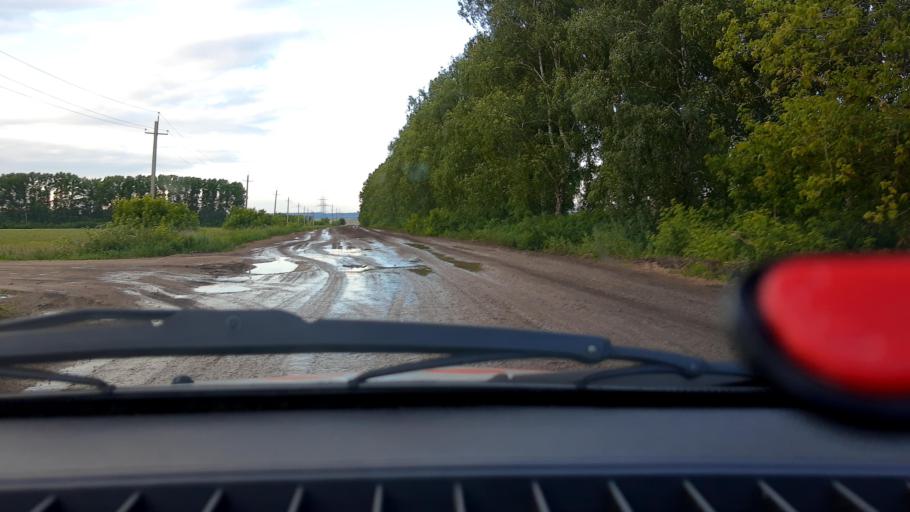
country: RU
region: Bashkortostan
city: Tolbazy
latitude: 54.1910
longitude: 55.8771
